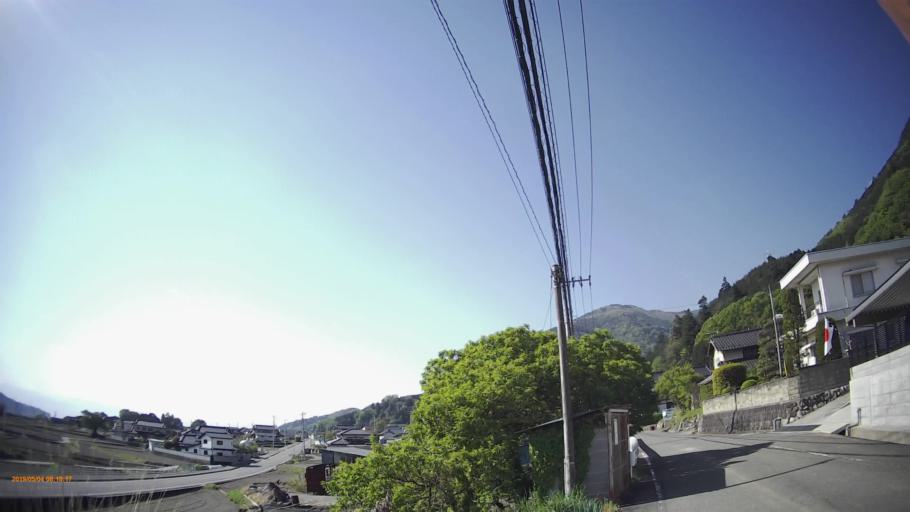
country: JP
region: Yamanashi
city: Nirasaki
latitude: 35.7358
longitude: 138.4089
